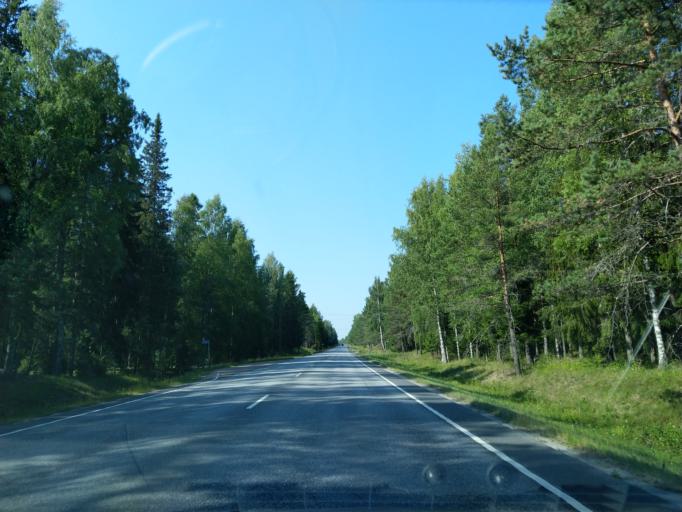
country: FI
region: Satakunta
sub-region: Pori
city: Noormarkku
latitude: 61.6245
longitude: 21.9171
